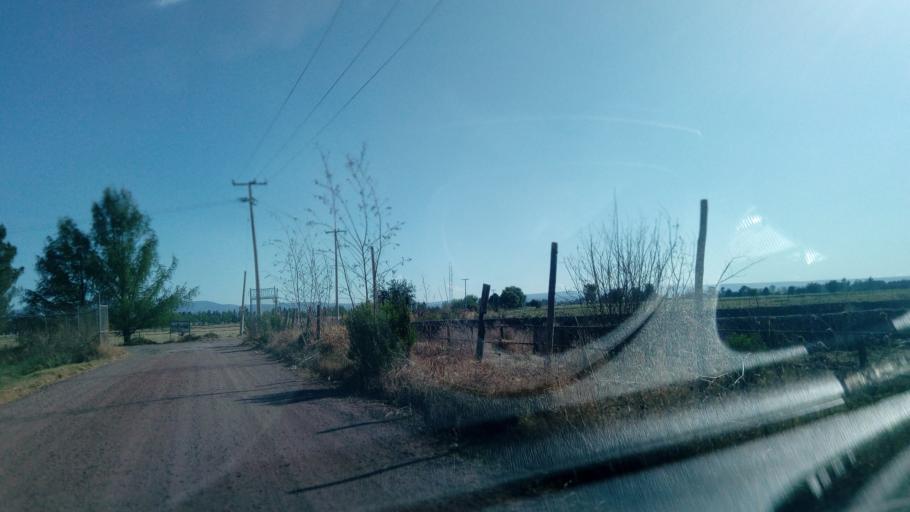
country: MX
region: Durango
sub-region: Durango
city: Jose Refugio Salcido
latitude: 24.0137
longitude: -104.5544
